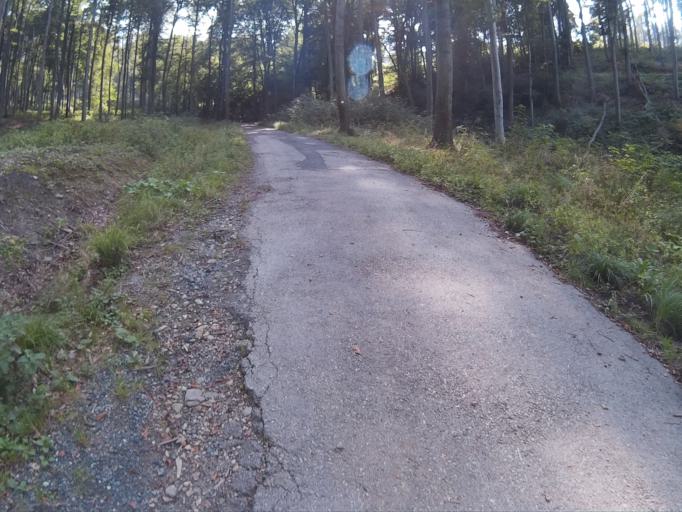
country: HU
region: Vas
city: Koszeg
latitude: 47.3860
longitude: 16.5002
